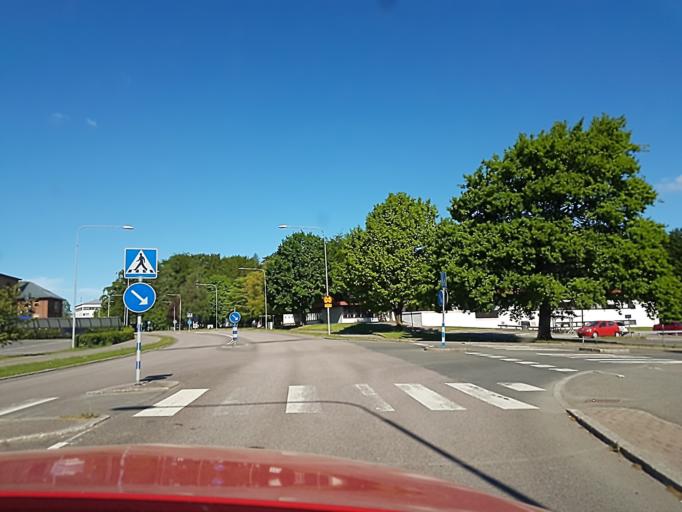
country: SE
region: Vaestra Goetaland
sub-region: Skovde Kommun
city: Skoevde
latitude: 58.3874
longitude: 13.8568
